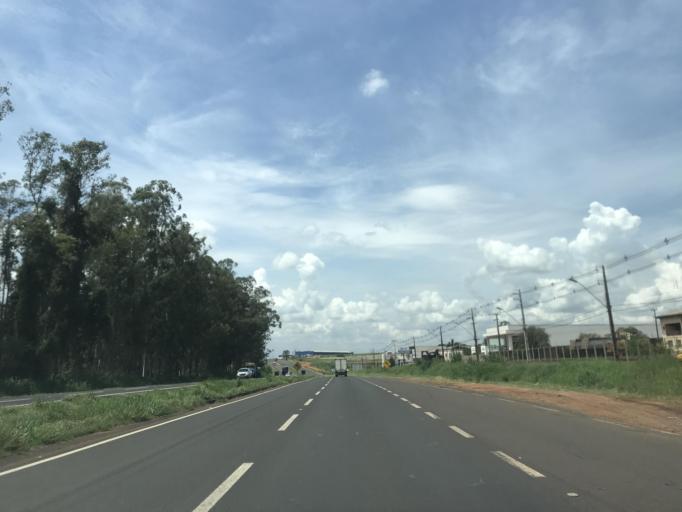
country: BR
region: Parana
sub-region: Alto Parana
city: Alto Parana
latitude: -23.2059
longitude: -52.1945
